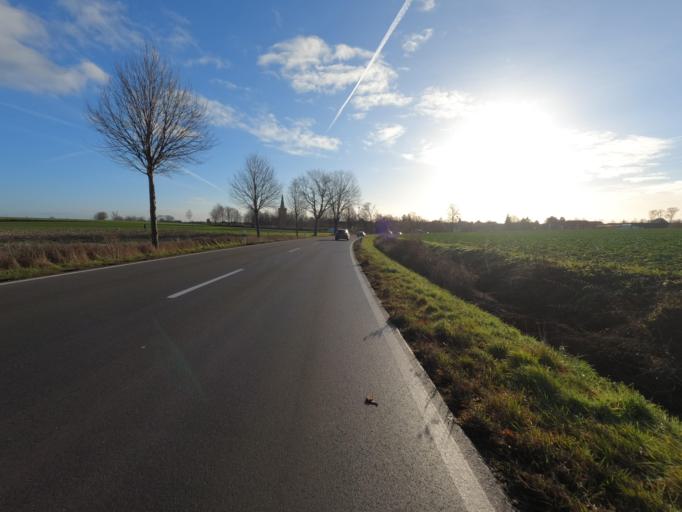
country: DE
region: North Rhine-Westphalia
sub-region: Regierungsbezirk Koln
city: Bedburg
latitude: 50.9676
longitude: 6.5344
